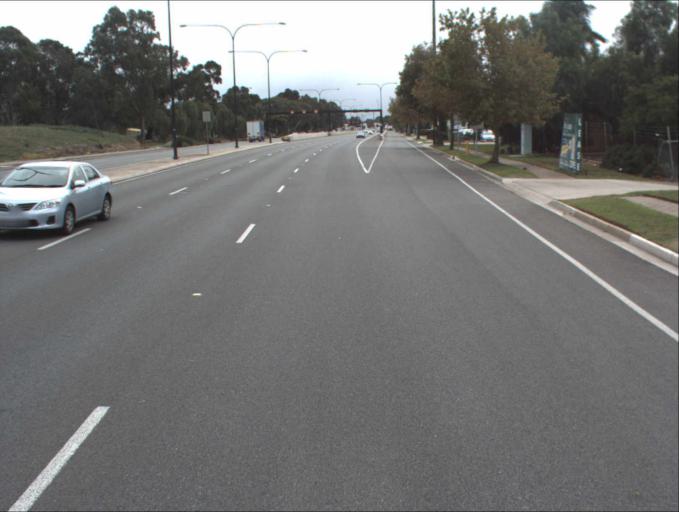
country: AU
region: South Australia
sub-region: Charles Sturt
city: Woodville
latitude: -34.8717
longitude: 138.5711
